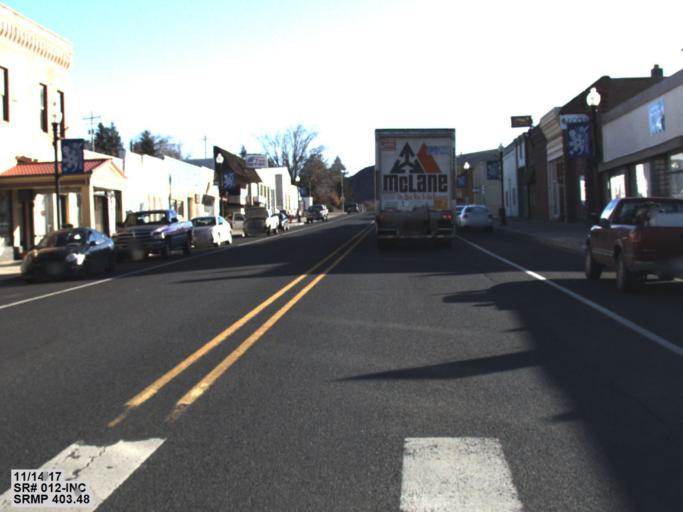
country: US
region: Washington
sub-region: Garfield County
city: Pomeroy
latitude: 46.4745
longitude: -117.5999
